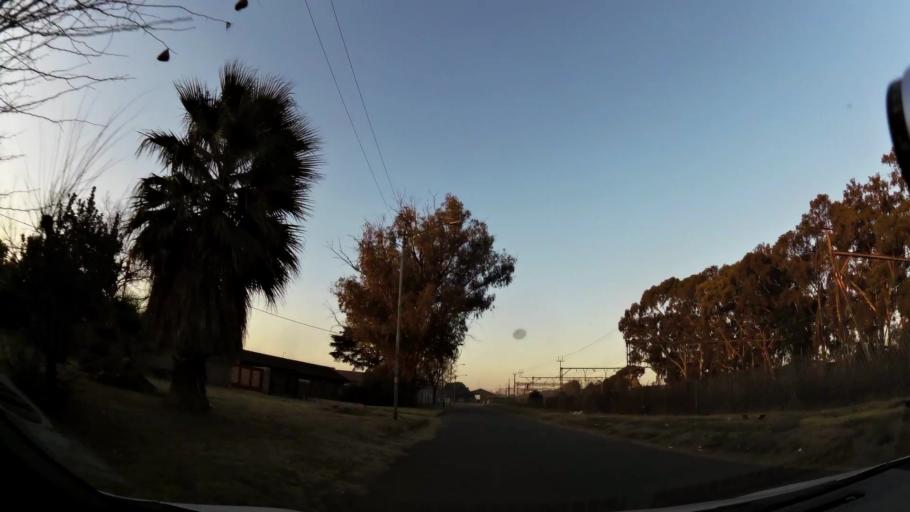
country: ZA
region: Gauteng
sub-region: Ekurhuleni Metropolitan Municipality
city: Germiston
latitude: -26.2733
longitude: 28.1588
